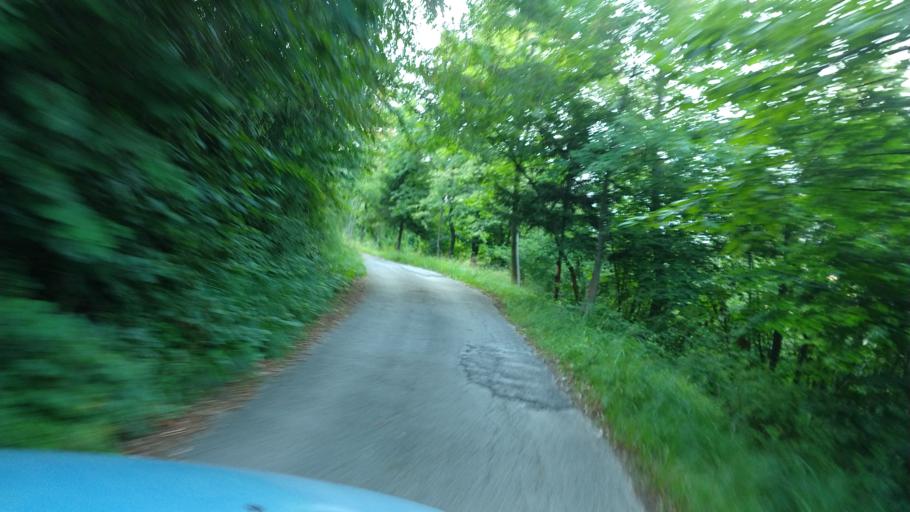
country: IT
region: Veneto
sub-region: Provincia di Vicenza
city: Campolongo sul Brenta
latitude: 45.8250
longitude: 11.6984
